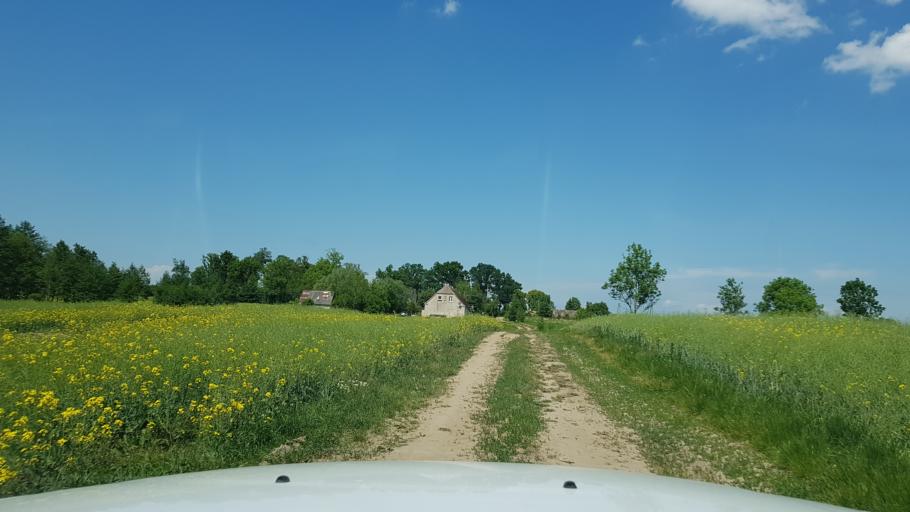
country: PL
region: West Pomeranian Voivodeship
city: Trzcinsko Zdroj
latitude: 52.9419
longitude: 14.5805
